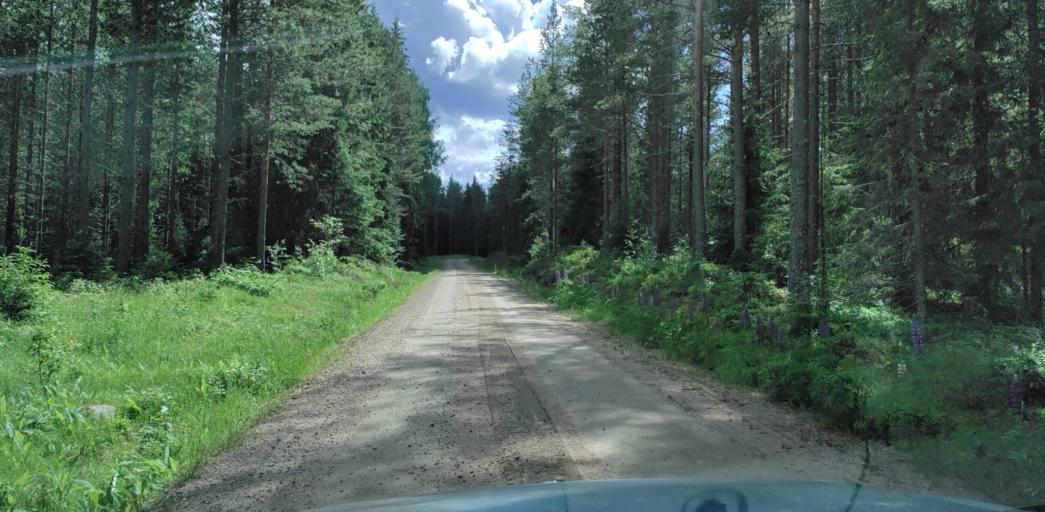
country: SE
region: Vaermland
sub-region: Hagfors Kommun
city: Ekshaerad
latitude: 60.0571
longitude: 13.3108
